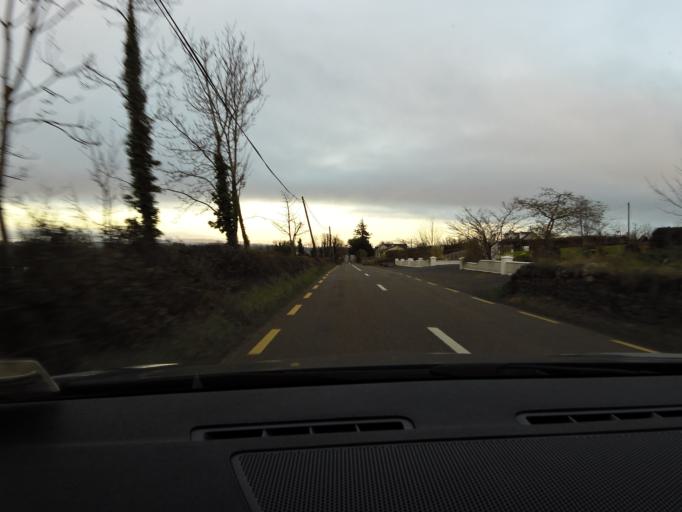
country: IE
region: Connaught
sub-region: Sligo
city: Ballymote
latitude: 53.9888
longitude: -8.4960
